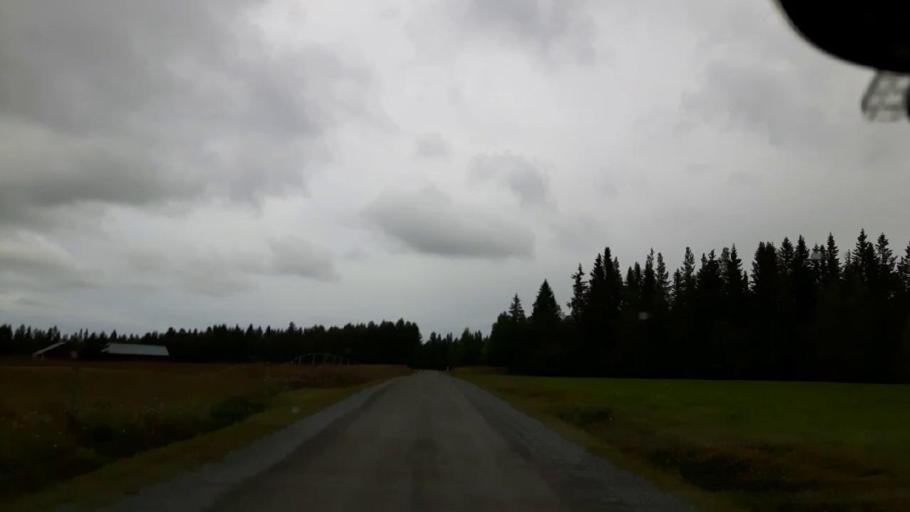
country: SE
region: Jaemtland
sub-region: OEstersunds Kommun
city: Ostersund
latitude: 63.0766
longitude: 14.5544
